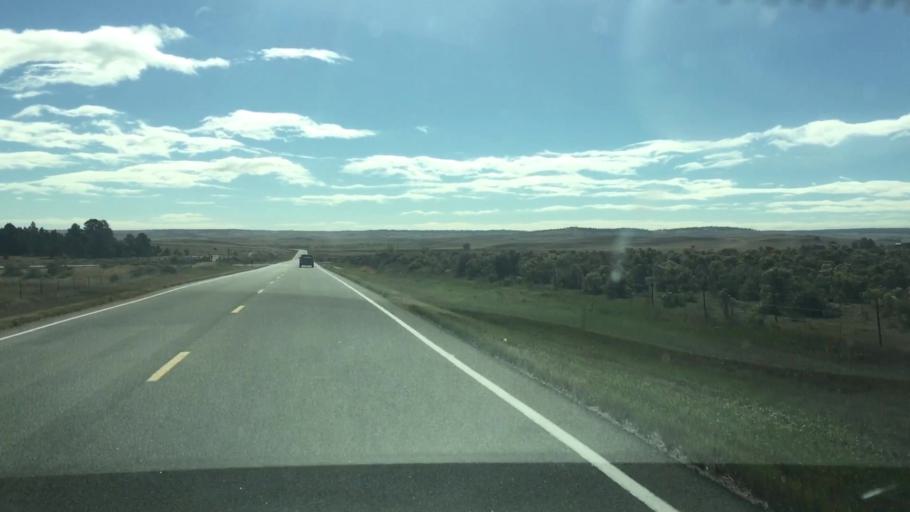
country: US
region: Colorado
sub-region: Elbert County
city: Kiowa
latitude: 39.3048
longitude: -104.3493
